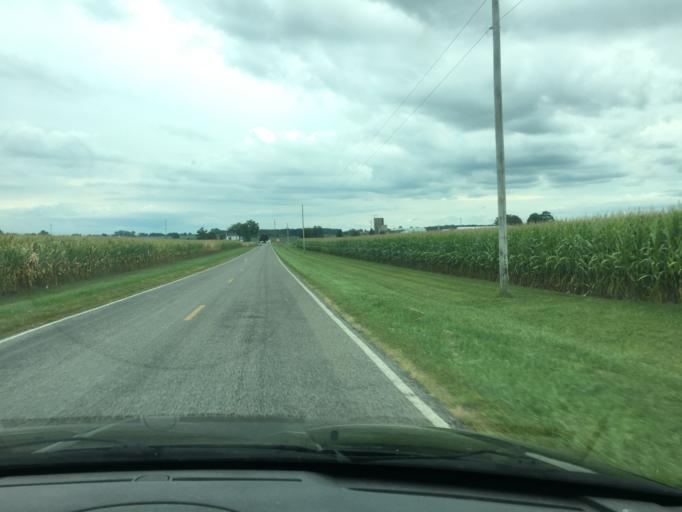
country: US
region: Ohio
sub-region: Logan County
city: West Liberty
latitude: 40.1916
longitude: -83.7475
